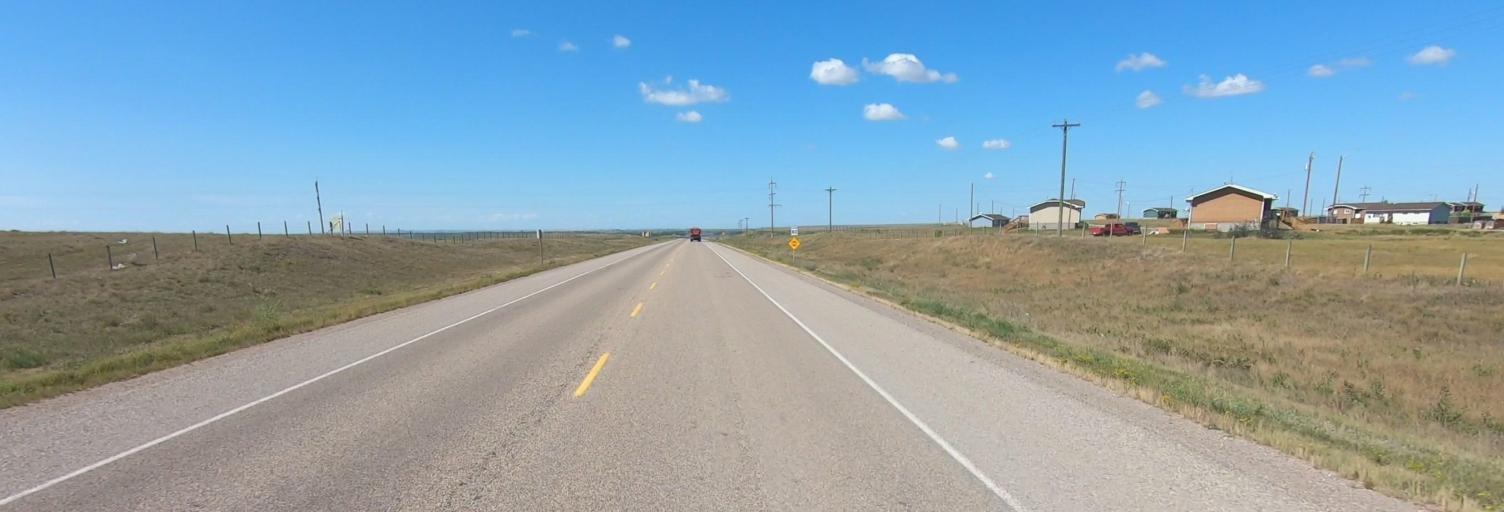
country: CA
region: Alberta
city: Strathmore
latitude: 50.8482
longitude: -113.0753
